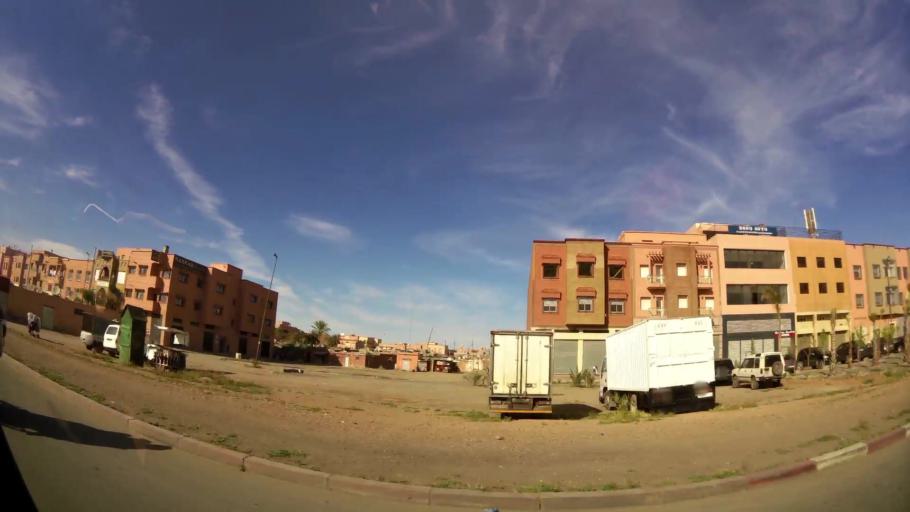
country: MA
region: Marrakech-Tensift-Al Haouz
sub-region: Marrakech
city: Marrakesh
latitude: 31.6702
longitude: -8.0398
